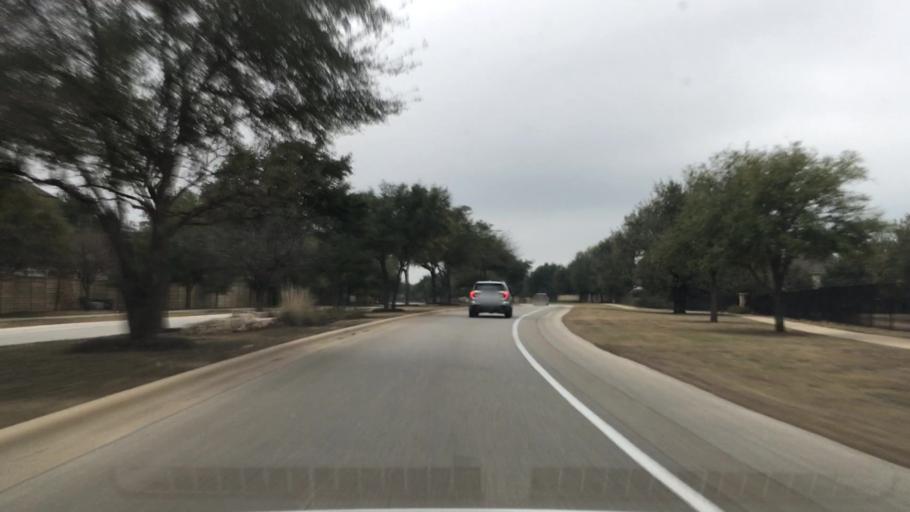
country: US
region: Texas
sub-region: Williamson County
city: Cedar Park
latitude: 30.4819
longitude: -97.8515
